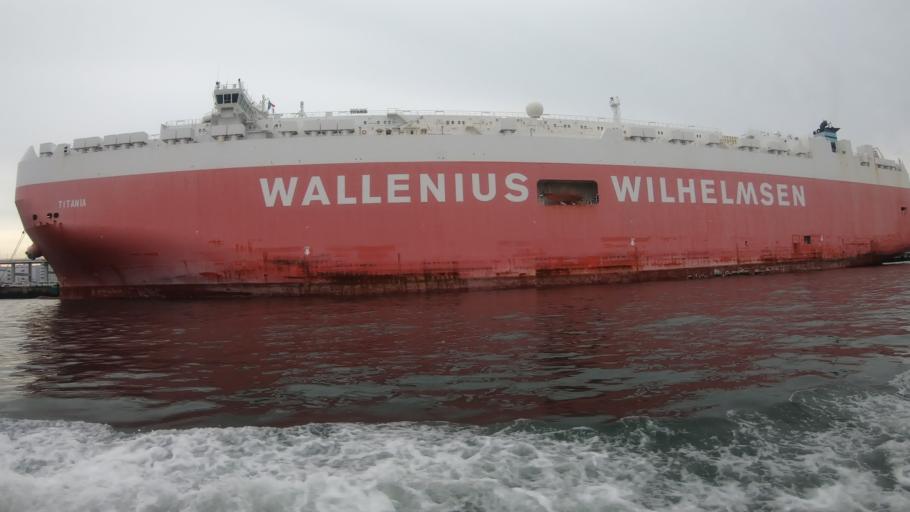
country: JP
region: Kanagawa
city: Yokohama
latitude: 35.4691
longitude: 139.6798
